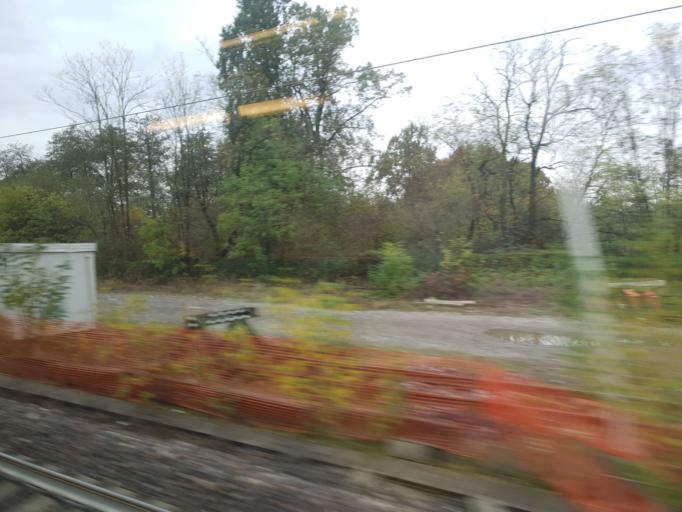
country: IT
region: Lombardy
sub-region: Provincia di Varese
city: Uboldo
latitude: 45.6268
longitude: 9.0041
